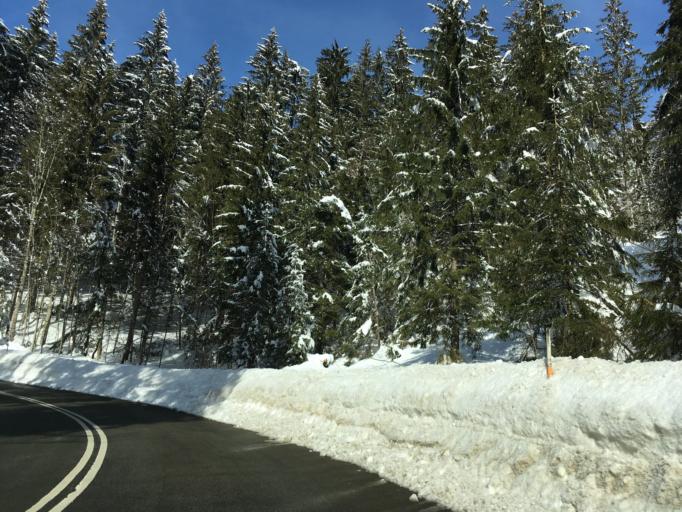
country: DE
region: Bavaria
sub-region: Upper Bavaria
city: Burg Unter-Falkenstein
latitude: 47.6726
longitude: 12.0778
